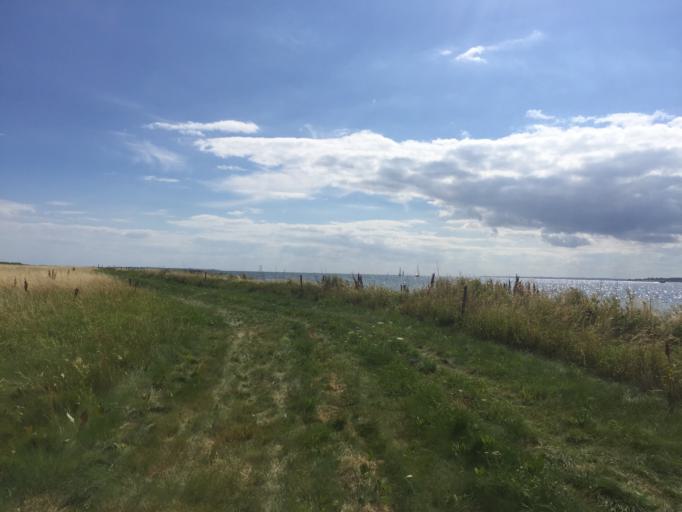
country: DK
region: South Denmark
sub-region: Faaborg-Midtfyn Kommune
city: Faaborg
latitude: 55.0701
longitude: 10.2346
